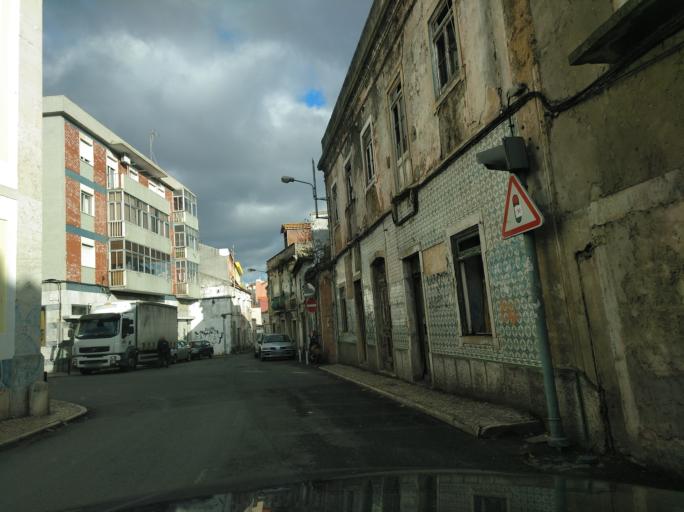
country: PT
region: Lisbon
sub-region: Loures
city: Sacavem
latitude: 38.7914
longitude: -9.1108
